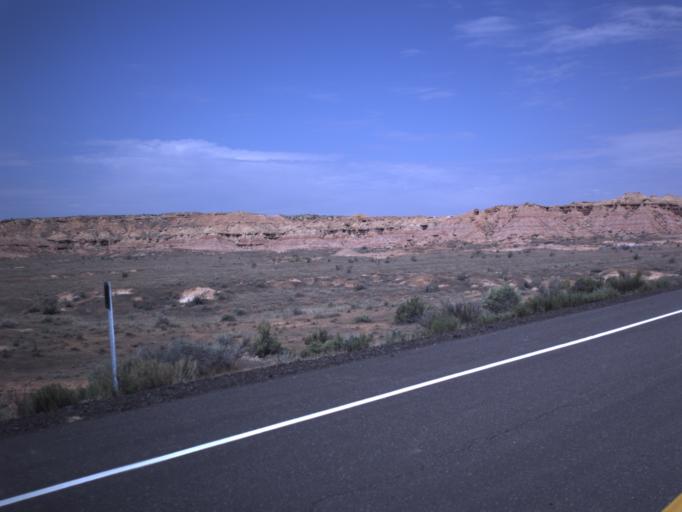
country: US
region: Utah
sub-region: Uintah County
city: Naples
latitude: 40.1224
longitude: -109.2576
